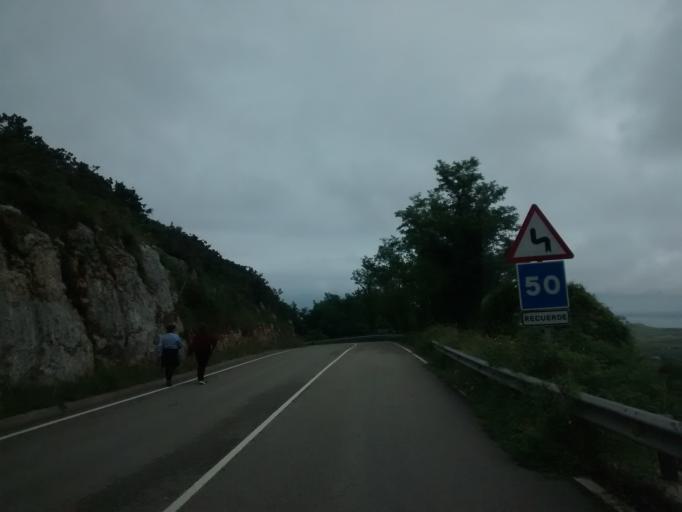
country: ES
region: Cantabria
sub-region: Provincia de Cantabria
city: Santillana
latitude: 43.4082
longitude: -4.1069
